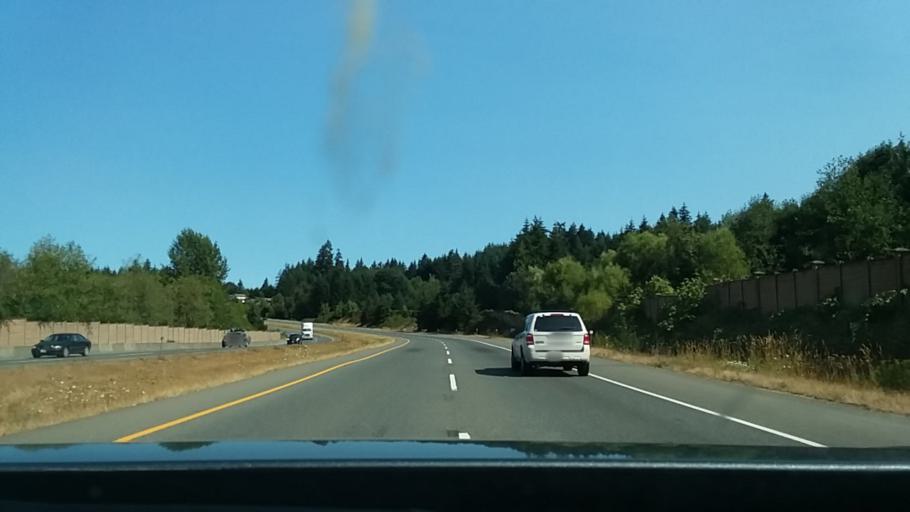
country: CA
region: British Columbia
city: Nanaimo
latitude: 49.2174
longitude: -124.0440
